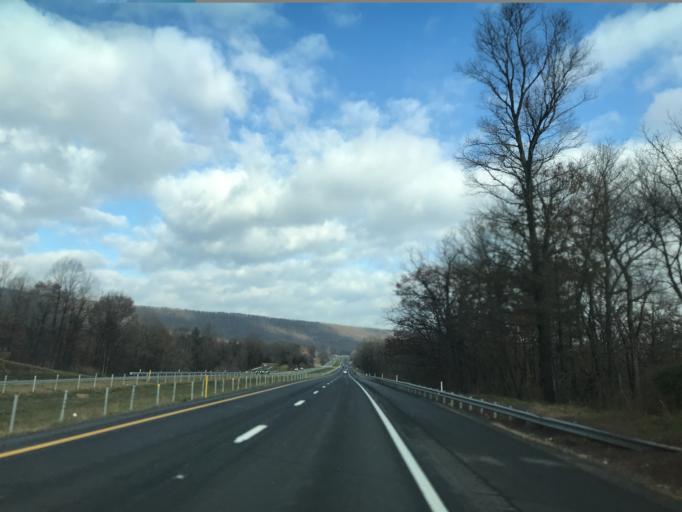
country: US
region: Maryland
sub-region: Washington County
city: Hancock
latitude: 39.8203
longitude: -78.2716
